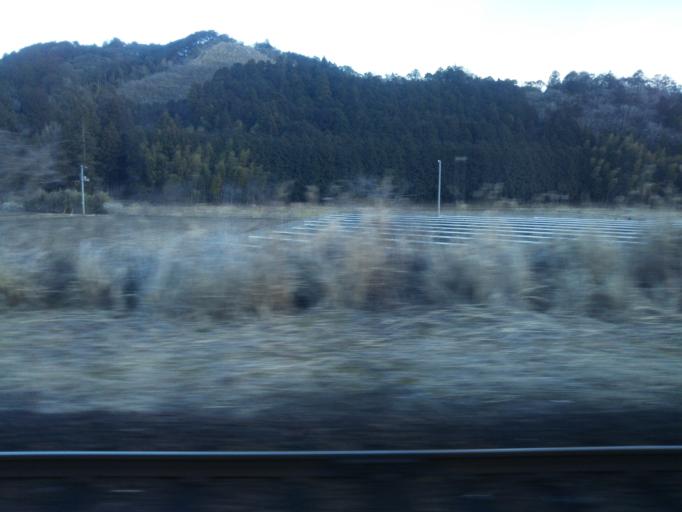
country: JP
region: Kochi
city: Susaki
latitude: 33.2762
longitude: 133.1756
